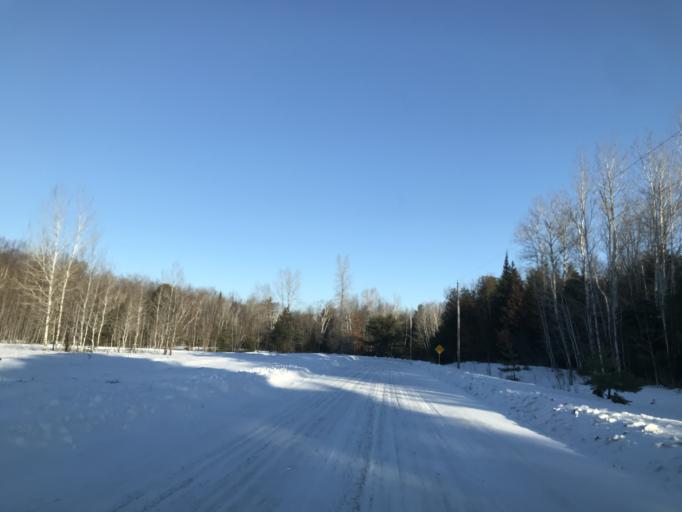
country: US
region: Michigan
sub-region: Menominee County
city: Menominee
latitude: 45.2926
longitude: -87.6953
